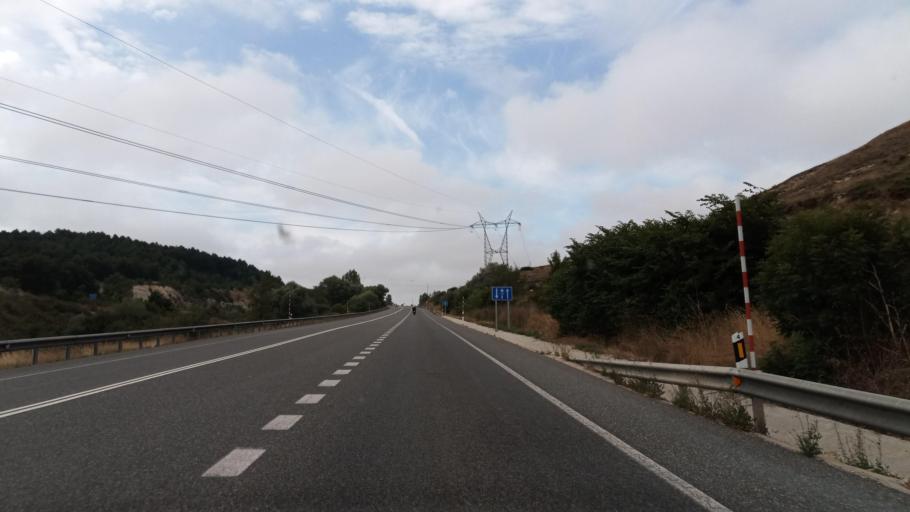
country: ES
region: Castille and Leon
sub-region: Provincia de Burgos
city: Monasterio de Rodilla
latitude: 42.4470
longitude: -3.4866
